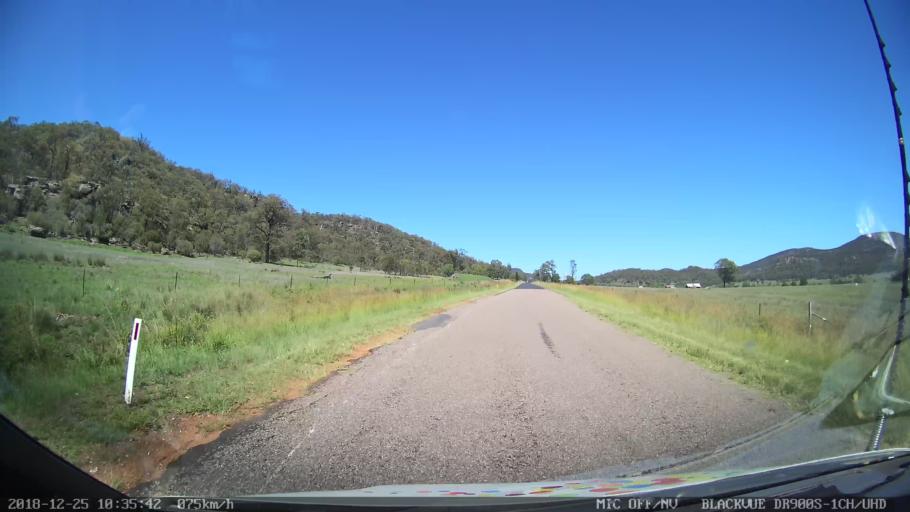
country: AU
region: New South Wales
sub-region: Upper Hunter Shire
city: Merriwa
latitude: -32.4015
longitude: 150.3941
